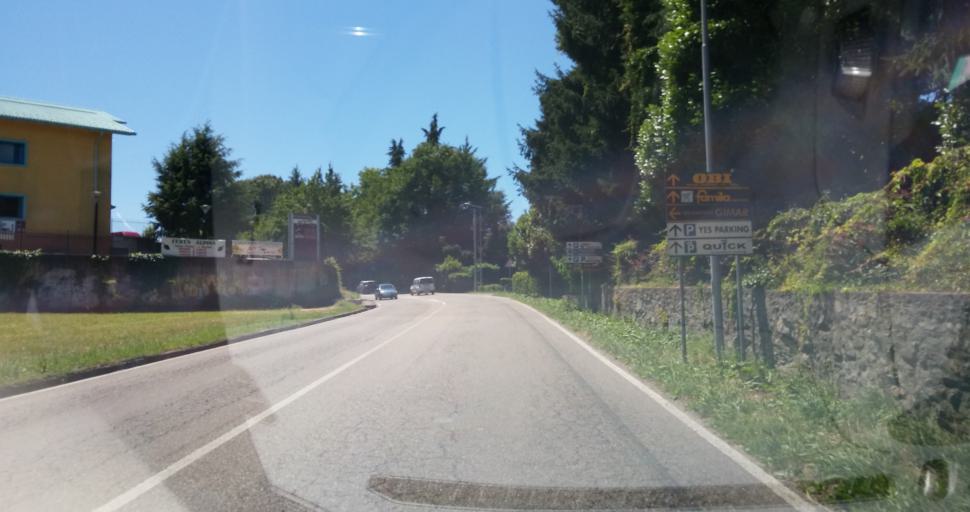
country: IT
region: Lombardy
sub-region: Provincia di Varese
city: Somma Lombardo
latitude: 45.6964
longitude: 8.7013
